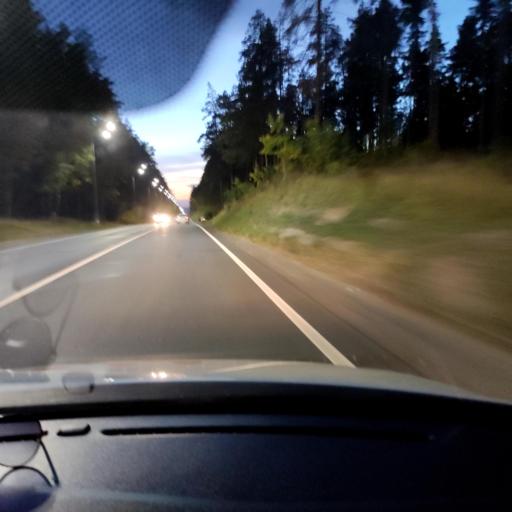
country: RU
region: Tatarstan
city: Verkhniy Uslon
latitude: 55.6373
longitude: 49.0535
